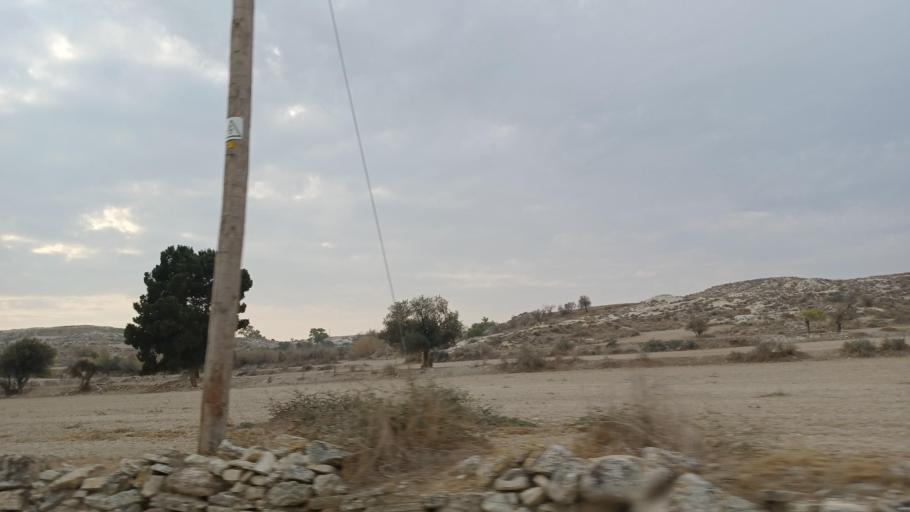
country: CY
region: Larnaka
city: Athienou
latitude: 35.0375
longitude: 33.5630
